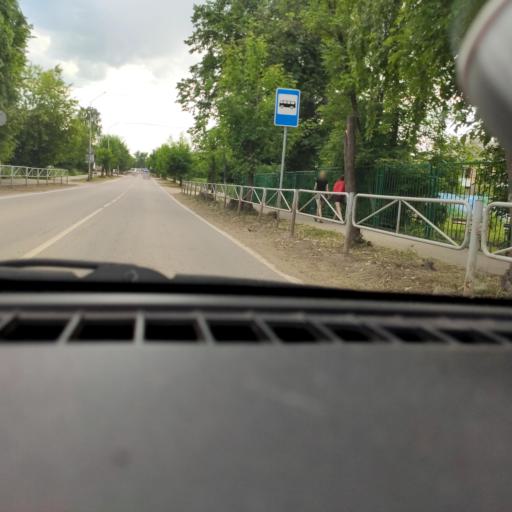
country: RU
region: Perm
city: Krasnokamsk
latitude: 58.0711
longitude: 55.8007
